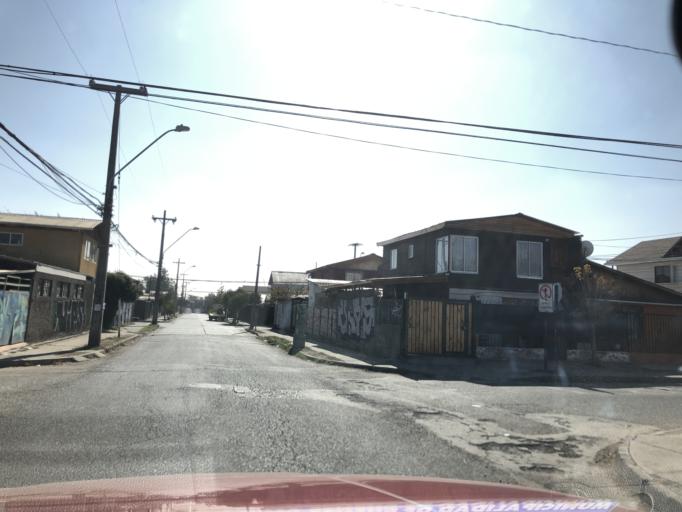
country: CL
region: Santiago Metropolitan
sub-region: Provincia de Cordillera
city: Puente Alto
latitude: -33.5676
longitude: -70.5765
